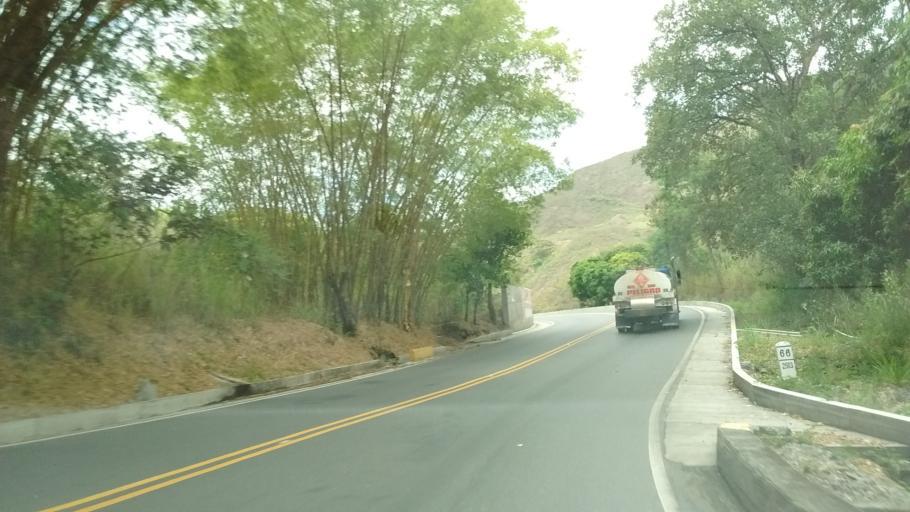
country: CO
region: Cauca
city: La Sierra
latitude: 2.1978
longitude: -76.8189
